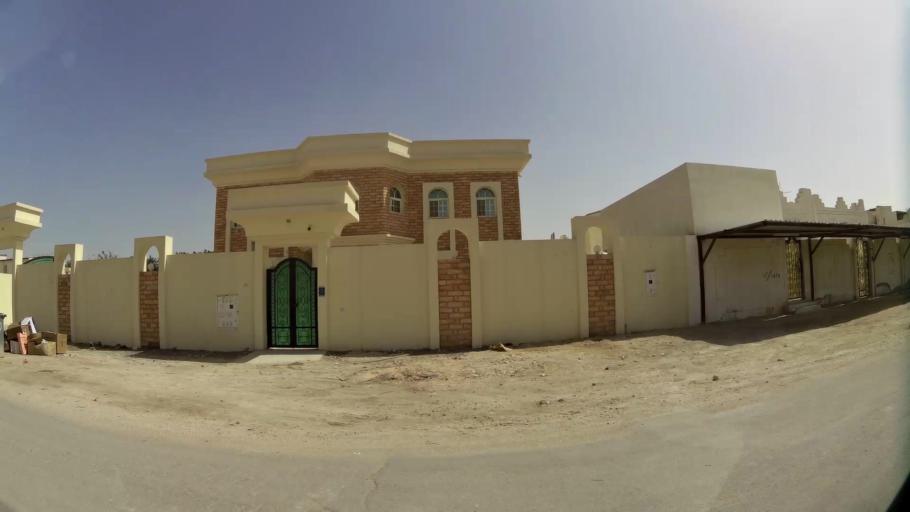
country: QA
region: Baladiyat Umm Salal
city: Umm Salal Muhammad
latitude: 25.3742
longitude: 51.4369
